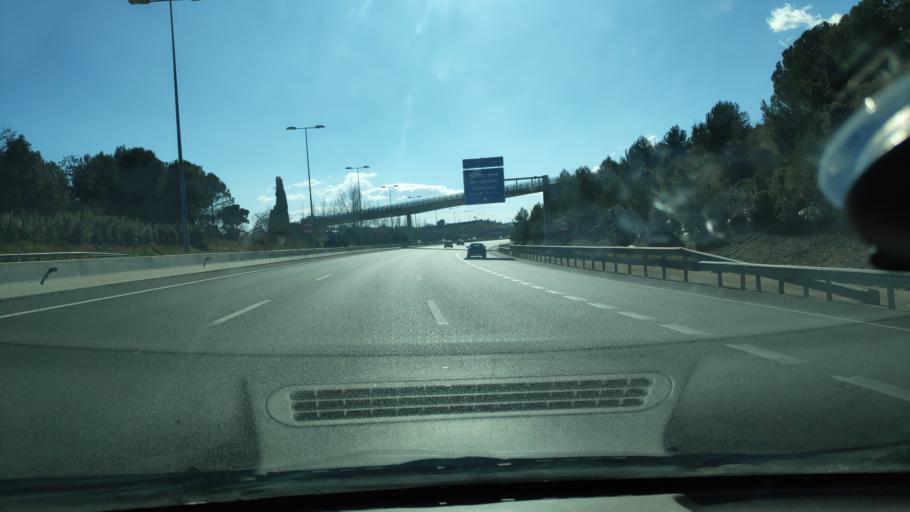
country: ES
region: Catalonia
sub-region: Provincia de Barcelona
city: Sant Quirze del Valles
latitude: 41.5575
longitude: 2.0784
